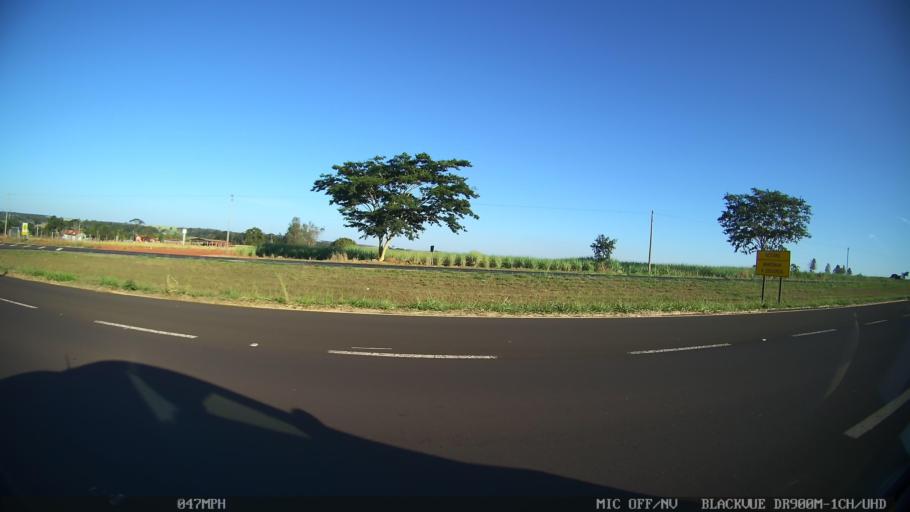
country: BR
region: Sao Paulo
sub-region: Guapiacu
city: Guapiacu
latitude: -20.7638
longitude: -49.1890
